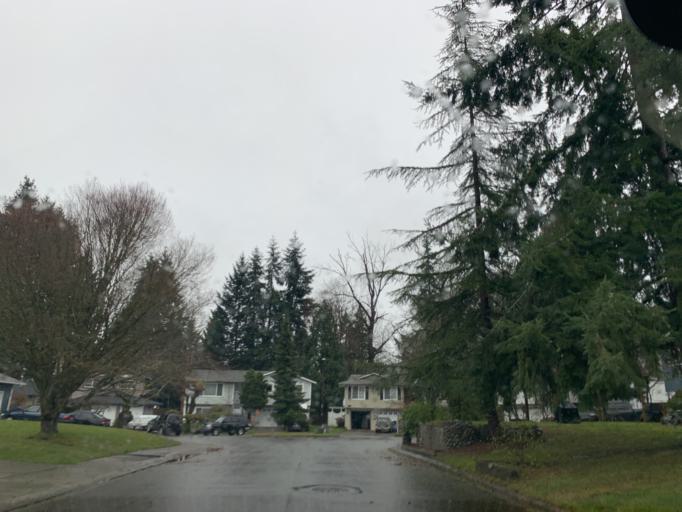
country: US
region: Washington
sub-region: King County
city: Kingsgate
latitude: 47.7350
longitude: -122.1678
